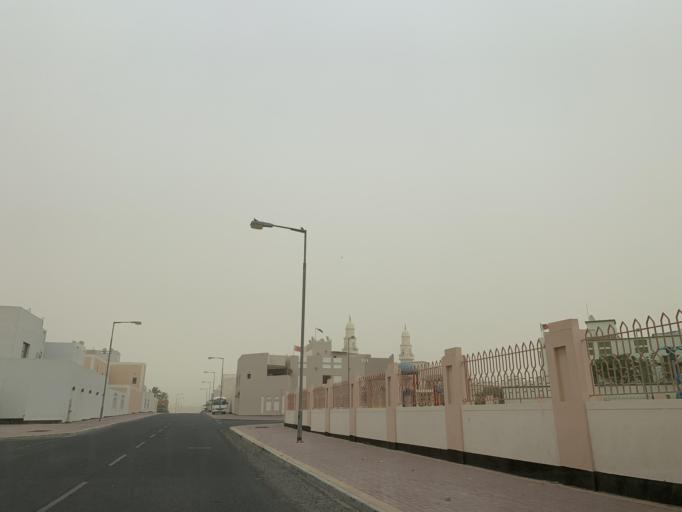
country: BH
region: Central Governorate
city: Madinat Hamad
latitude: 26.1298
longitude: 50.5112
